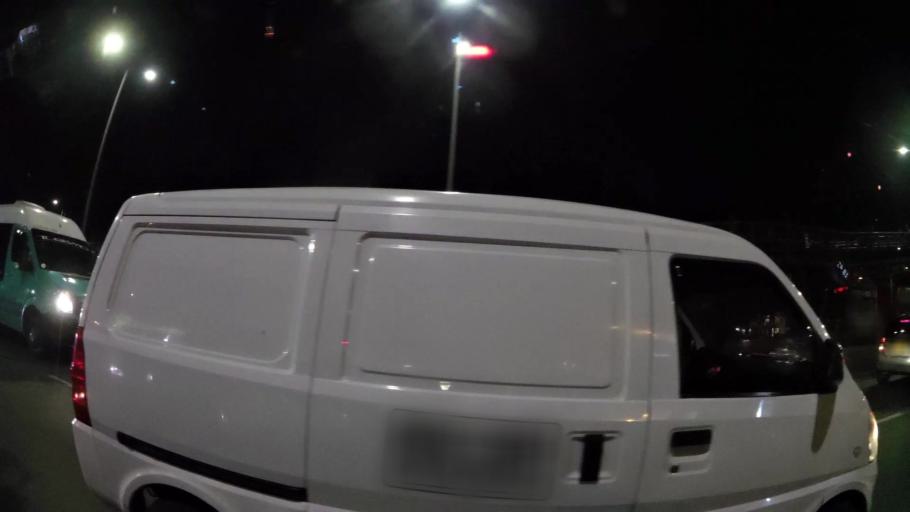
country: CO
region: Bogota D.C.
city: Bogota
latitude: 4.5945
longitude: -74.1349
